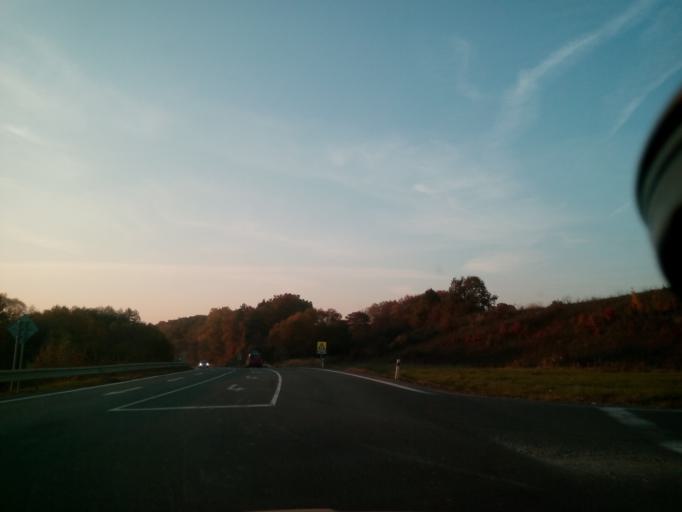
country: SK
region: Presovsky
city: Sabinov
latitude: 49.0026
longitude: 21.1029
